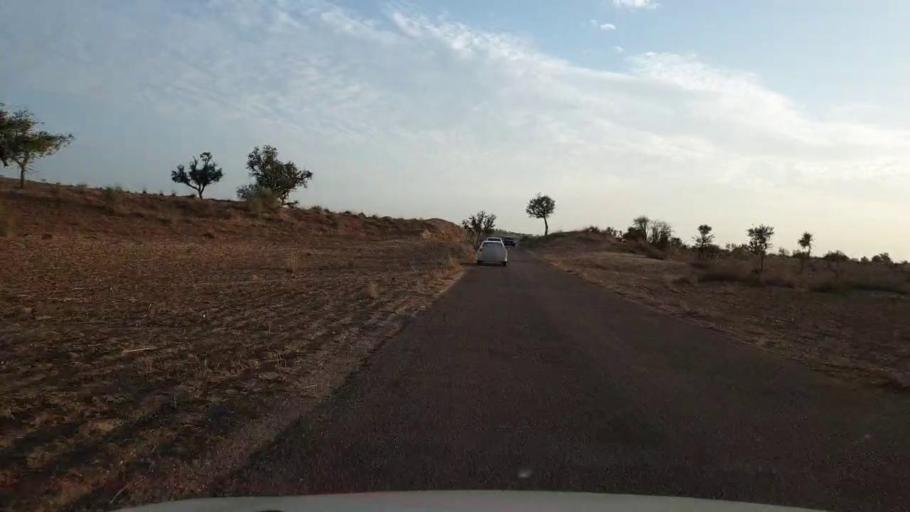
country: PK
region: Sindh
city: Nabisar
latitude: 25.0361
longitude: 69.9520
